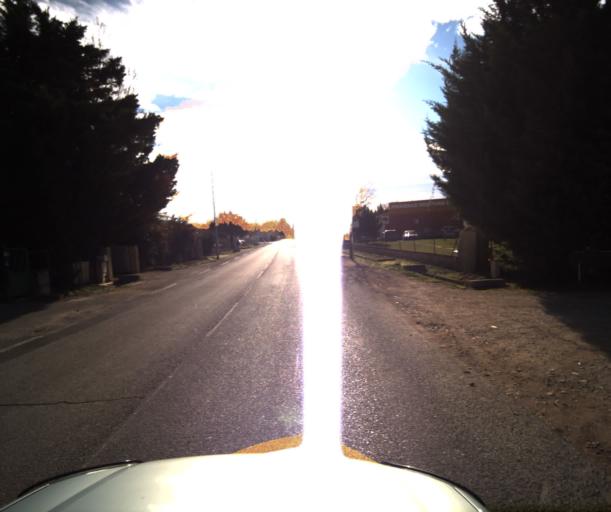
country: FR
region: Provence-Alpes-Cote d'Azur
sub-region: Departement du Vaucluse
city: Pertuis
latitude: 43.6752
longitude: 5.5029
